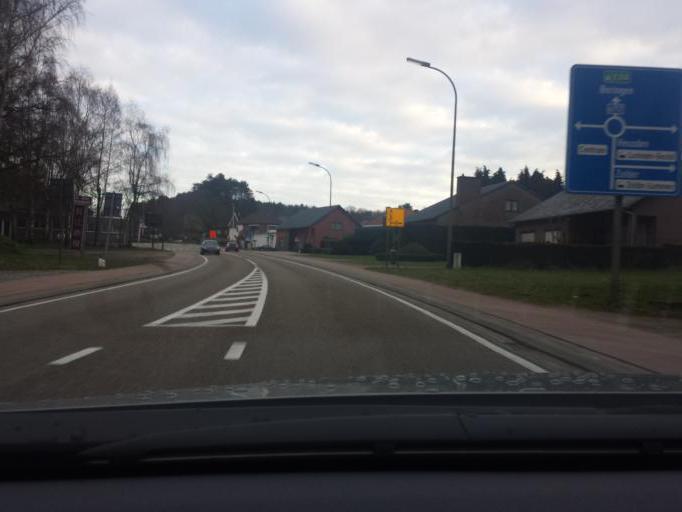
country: BE
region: Flanders
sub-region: Provincie Limburg
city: Lummen
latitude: 50.9868
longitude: 5.1985
